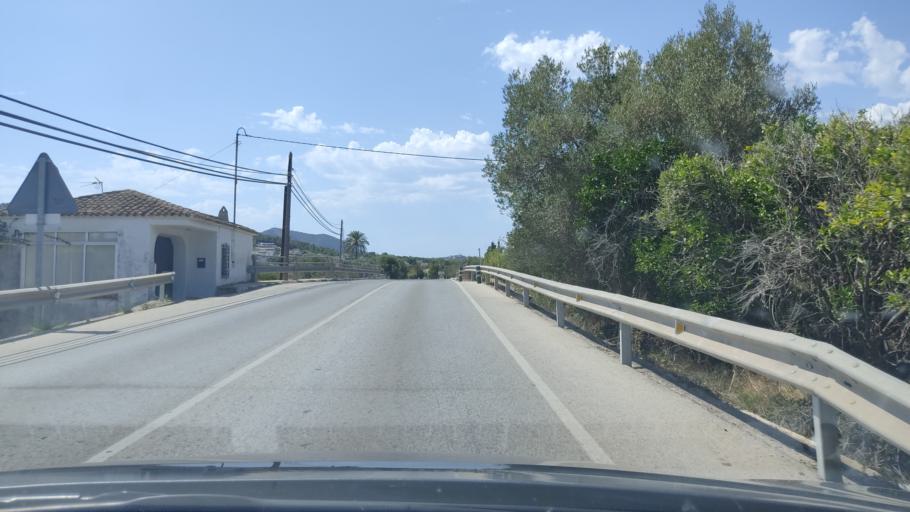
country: ES
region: Valencia
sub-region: Provincia de Alicante
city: Javea
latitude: 38.7774
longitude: 0.1509
